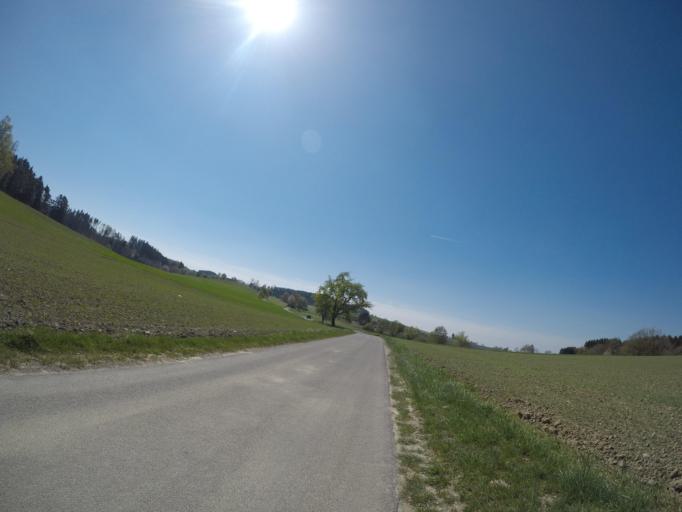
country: DE
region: Baden-Wuerttemberg
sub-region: Tuebingen Region
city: Markdorf
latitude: 47.7578
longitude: 9.3978
